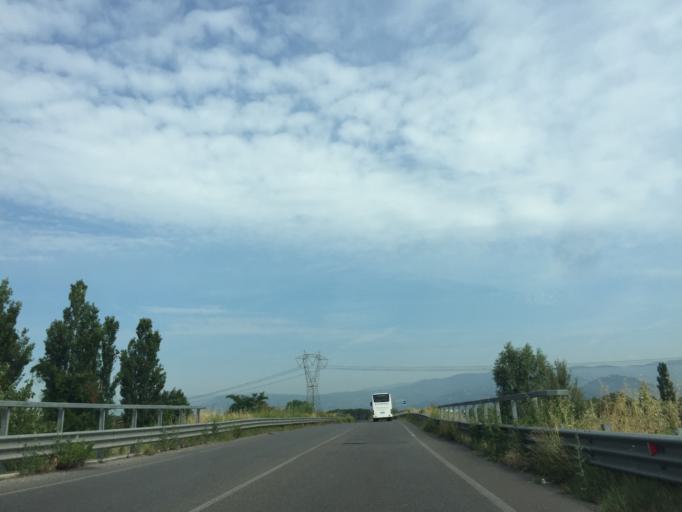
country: IT
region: Tuscany
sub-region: Provincia di Pistoia
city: Cintolese
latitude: 43.8467
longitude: 10.8125
